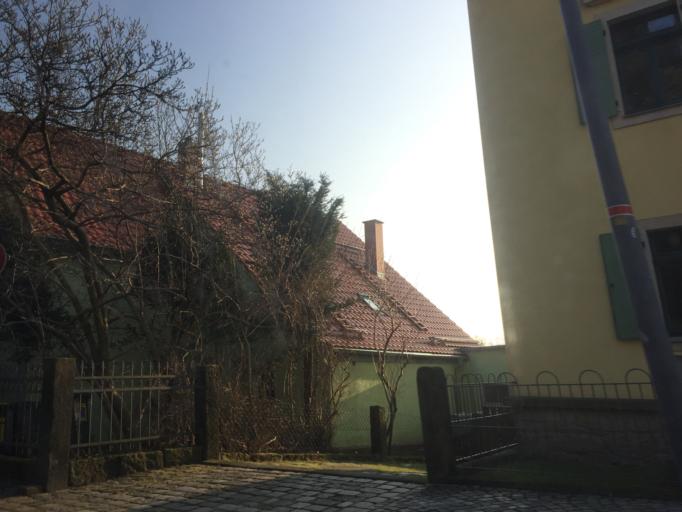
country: DE
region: Saxony
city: Heidenau
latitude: 51.0269
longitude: 13.8495
